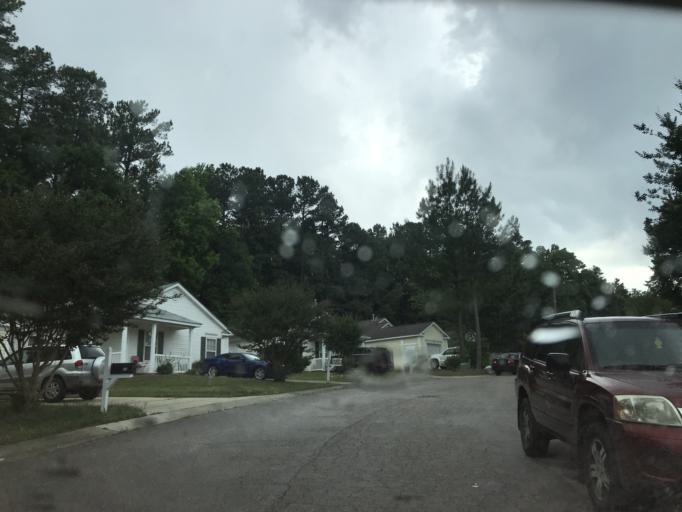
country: US
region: North Carolina
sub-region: Wake County
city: Knightdale
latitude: 35.8439
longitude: -78.5567
